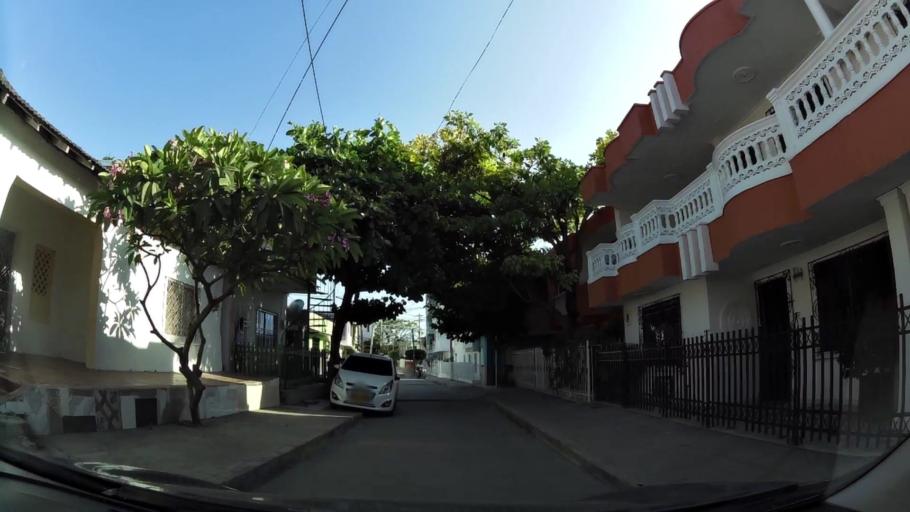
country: CO
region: Bolivar
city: Cartagena
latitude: 10.4026
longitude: -75.4843
